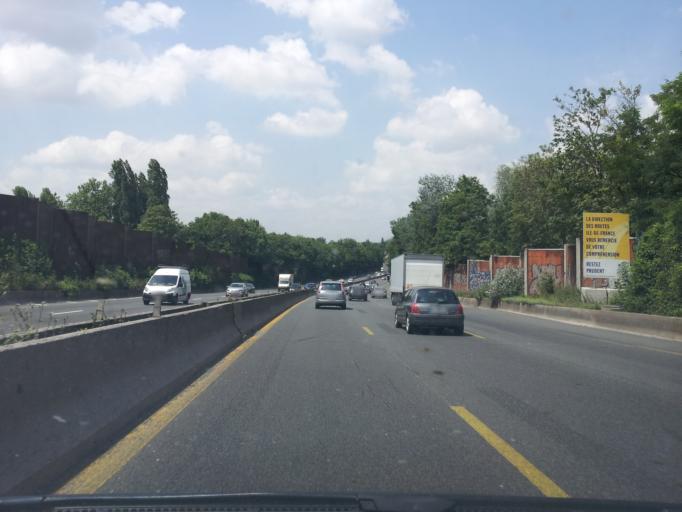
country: FR
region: Ile-de-France
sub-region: Departement de l'Essonne
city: Morsang-sur-Orge
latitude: 48.6683
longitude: 2.3545
